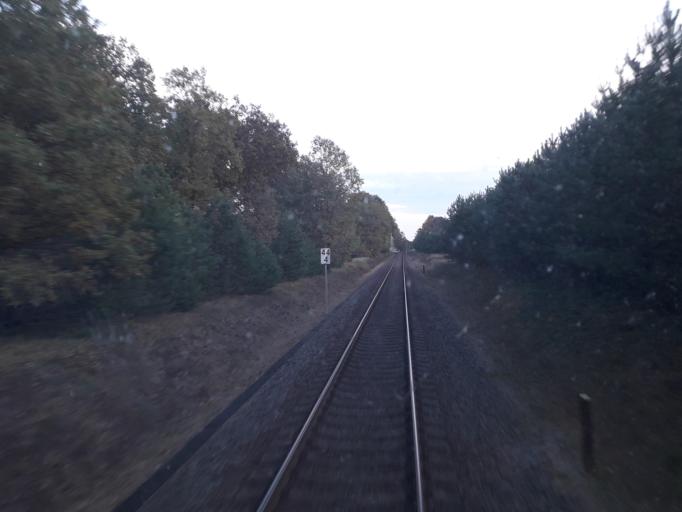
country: DE
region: Brandenburg
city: Walsleben
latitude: 52.9978
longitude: 12.6250
